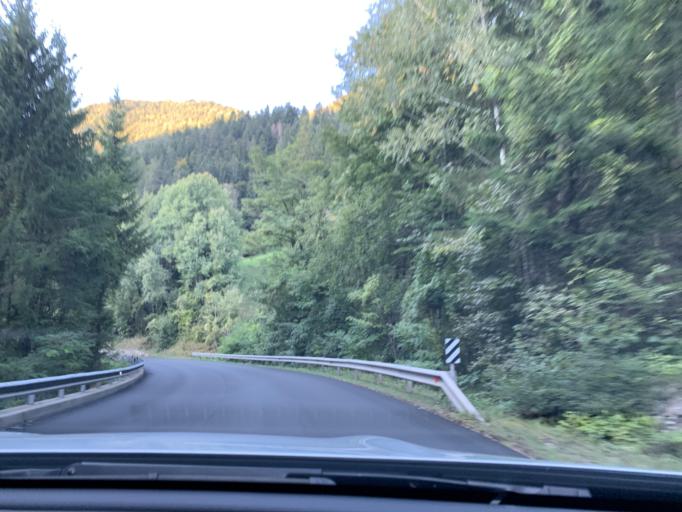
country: IT
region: Trentino-Alto Adige
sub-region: Bolzano
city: Nova Ponente
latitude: 46.4416
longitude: 11.4645
